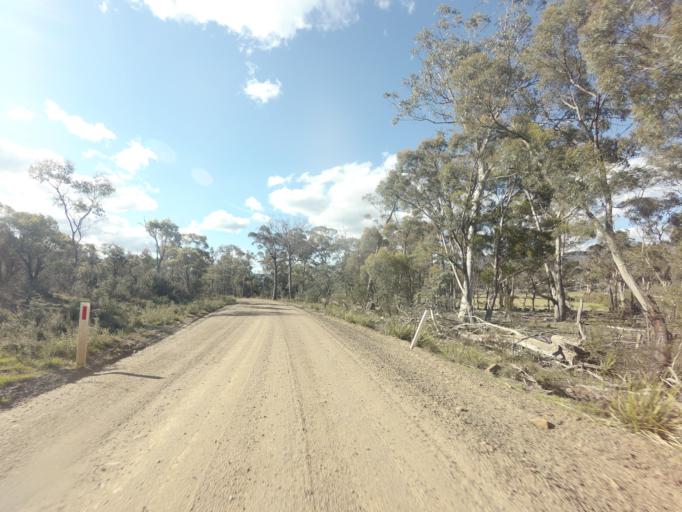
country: AU
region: Tasmania
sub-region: Break O'Day
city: St Helens
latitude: -41.8341
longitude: 148.0169
